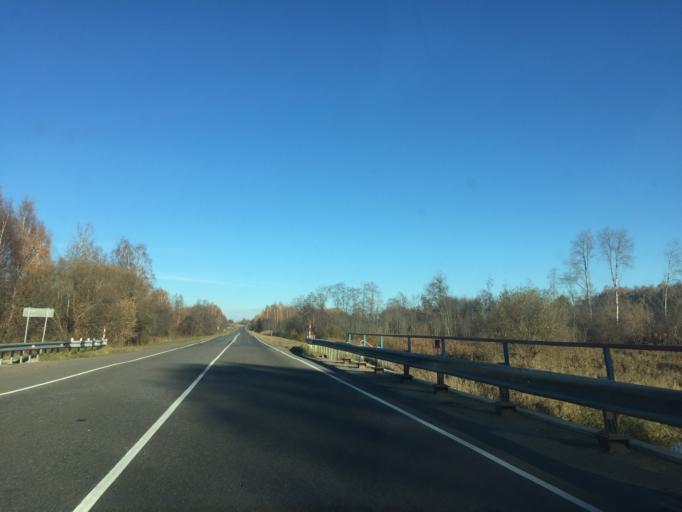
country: BY
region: Vitebsk
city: Navapolatsk
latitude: 55.3724
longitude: 28.3906
